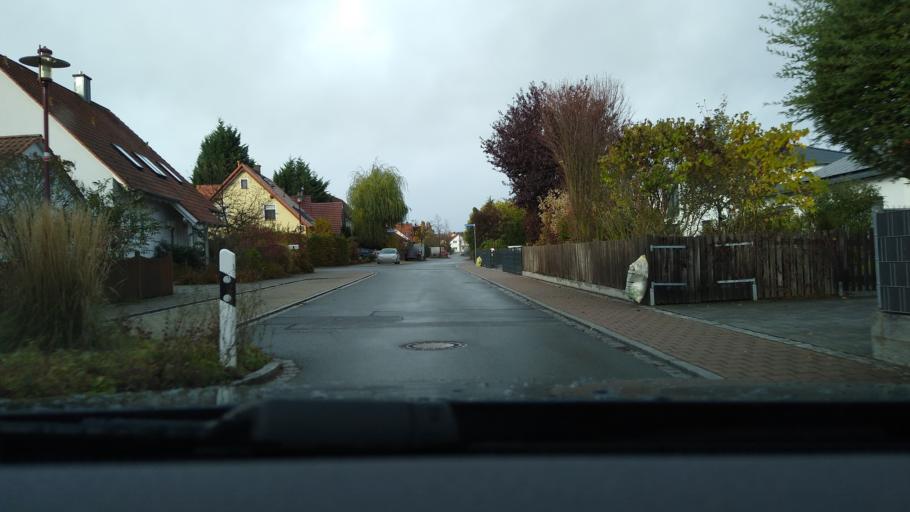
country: DE
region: Bavaria
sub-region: Regierungsbezirk Mittelfranken
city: Obermichelbach
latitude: 49.5302
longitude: 10.9074
